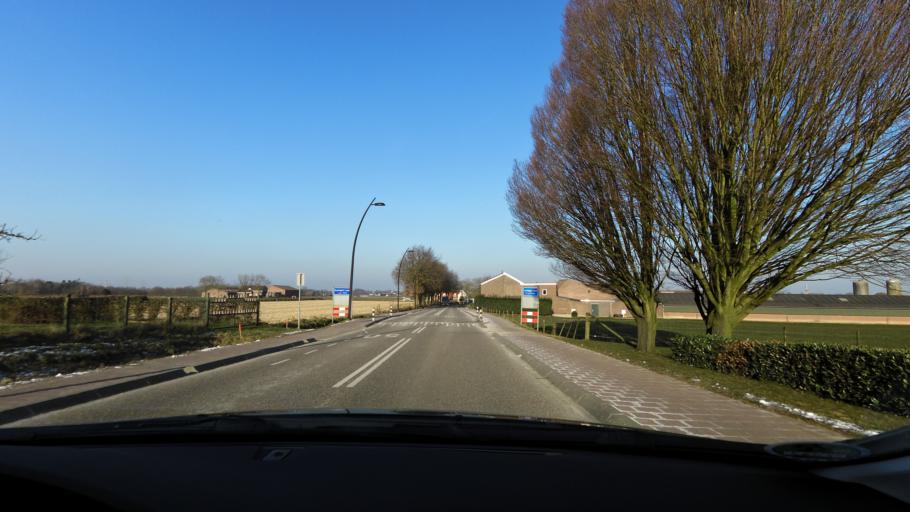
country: NL
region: Limburg
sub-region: Valkenburg aan de Geul
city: Valkenburg
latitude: 50.8909
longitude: 5.8401
